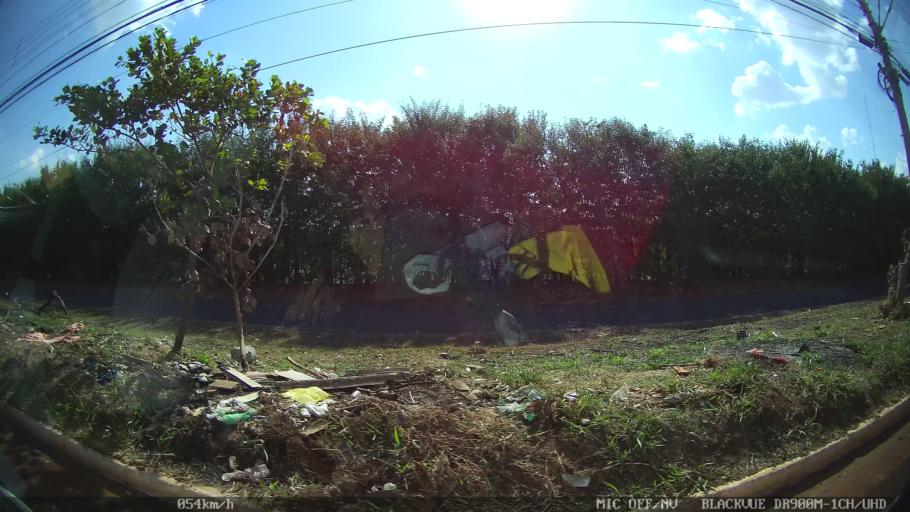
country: BR
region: Sao Paulo
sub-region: Ribeirao Preto
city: Ribeirao Preto
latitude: -21.2004
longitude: -47.8569
